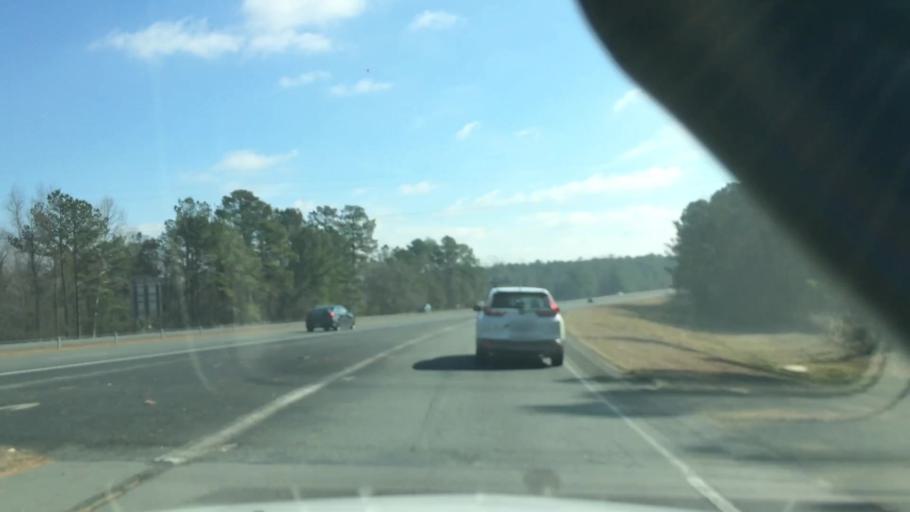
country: US
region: North Carolina
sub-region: Duplin County
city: Wallace
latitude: 34.7525
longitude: -77.9486
